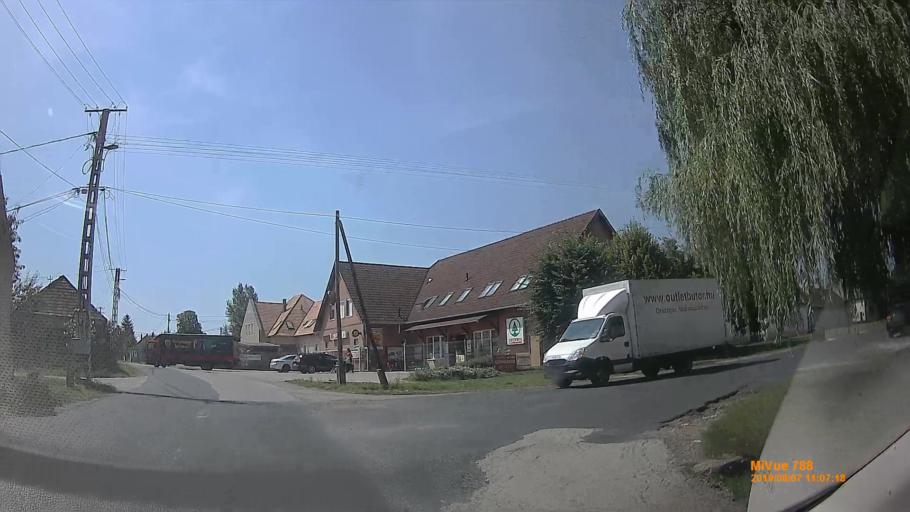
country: HU
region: Veszprem
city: Devecser
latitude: 47.0056
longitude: 17.4547
